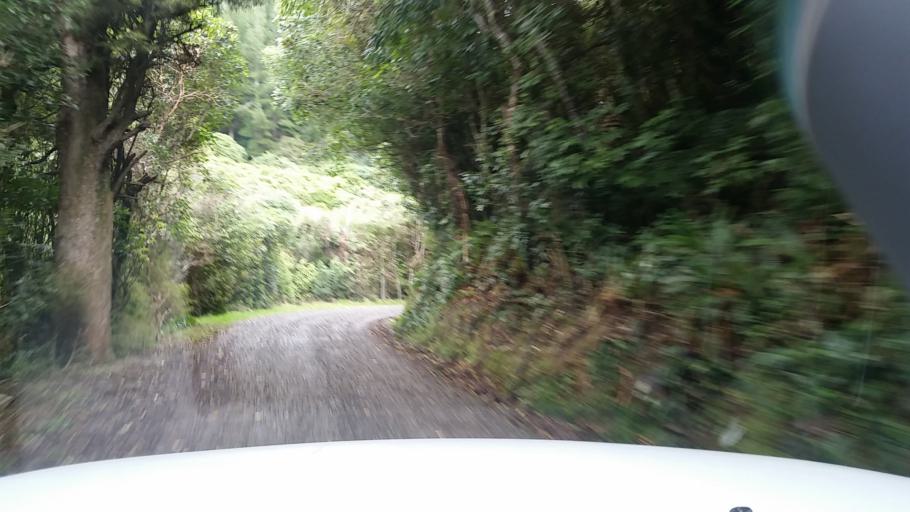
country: NZ
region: Canterbury
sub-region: Christchurch City
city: Christchurch
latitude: -43.6956
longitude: 172.7805
